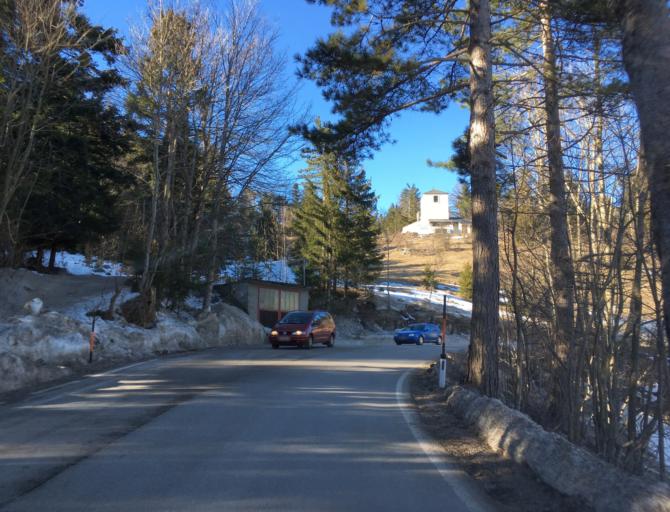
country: AT
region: Lower Austria
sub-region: Politischer Bezirk Wiener Neustadt
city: Waldegg
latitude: 47.8385
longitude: 16.0570
